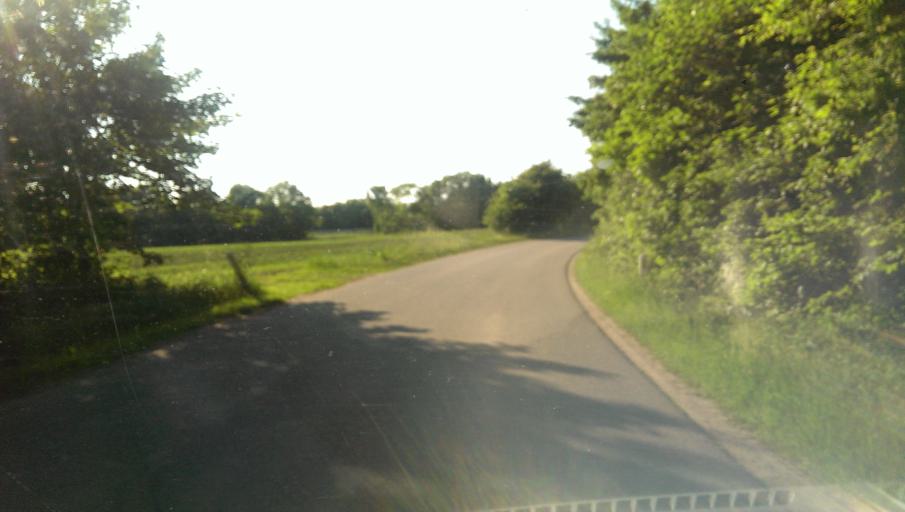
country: DK
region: South Denmark
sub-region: Esbjerg Kommune
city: Bramming
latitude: 55.5689
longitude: 8.6709
